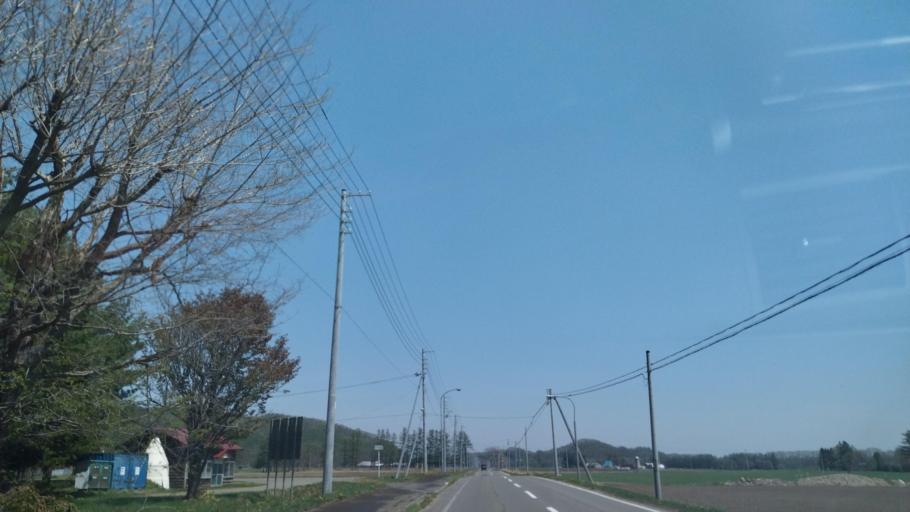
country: JP
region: Hokkaido
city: Obihiro
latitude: 42.8135
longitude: 142.9714
